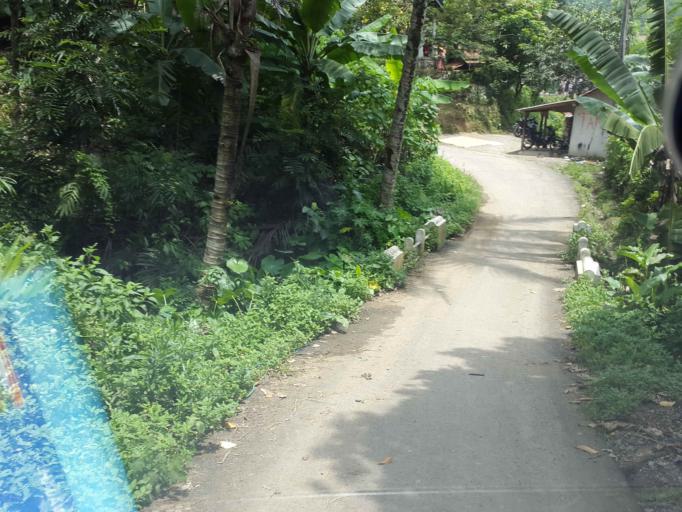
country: ID
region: Central Java
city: Muara
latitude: -7.2583
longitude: 108.8854
